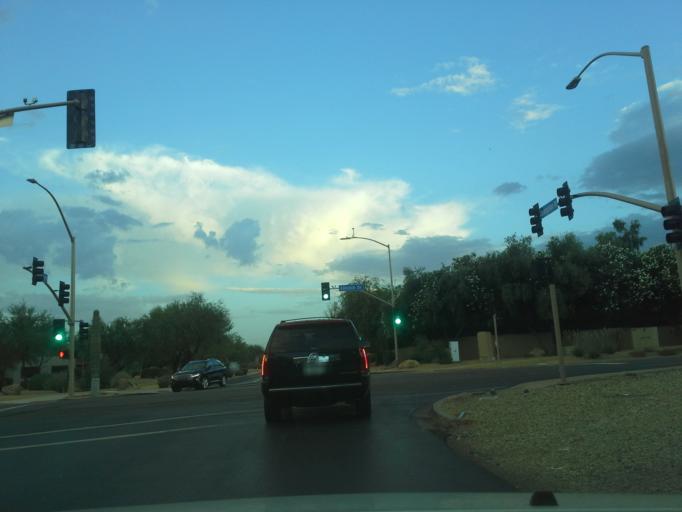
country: US
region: Arizona
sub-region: Maricopa County
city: Paradise Valley
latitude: 33.5314
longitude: -111.9432
